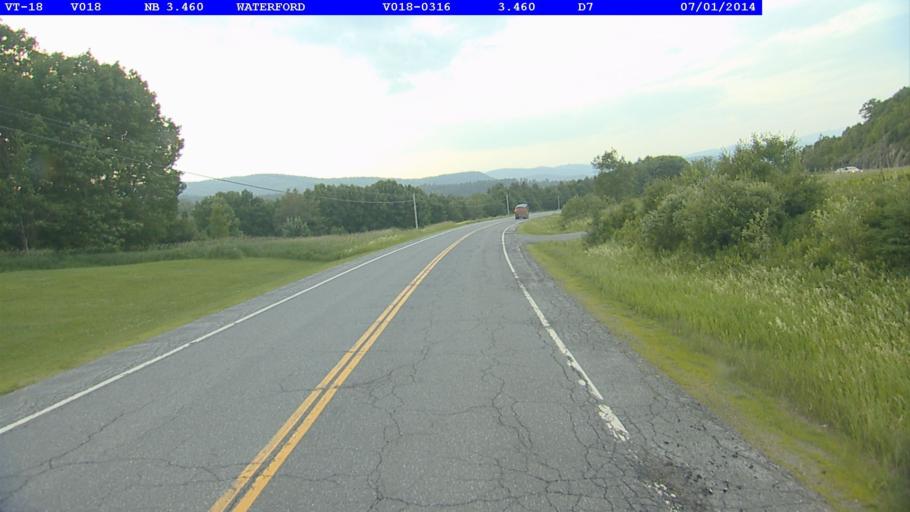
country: US
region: Vermont
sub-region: Caledonia County
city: Saint Johnsbury
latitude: 44.3816
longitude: -71.9229
